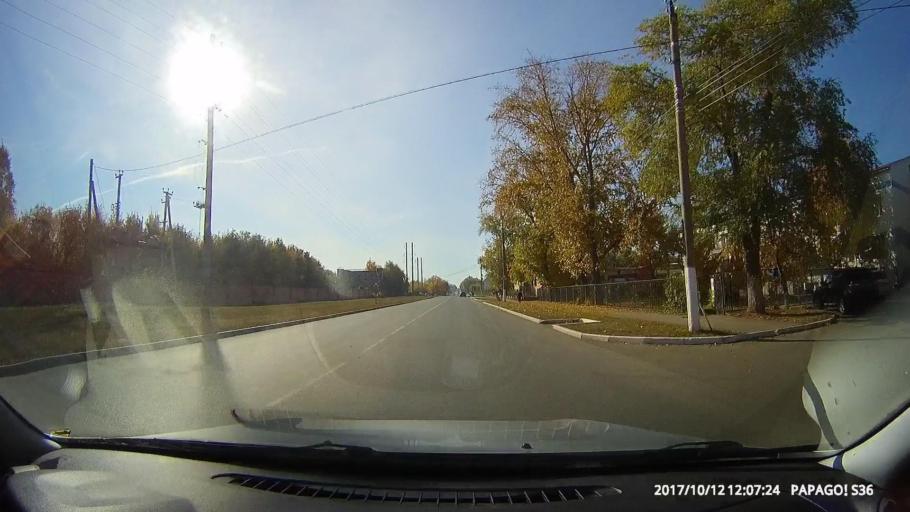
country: RU
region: Samara
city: Chapayevsk
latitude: 52.9673
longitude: 49.7014
